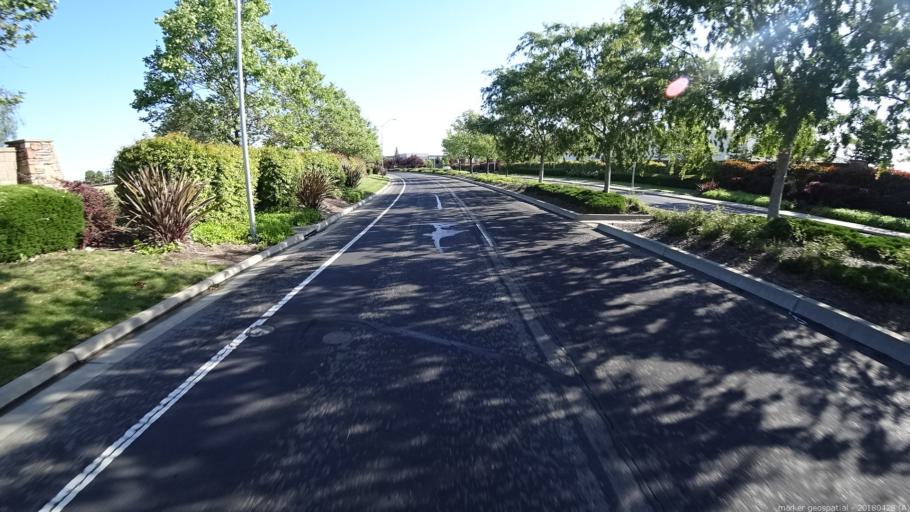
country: US
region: California
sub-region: Yolo County
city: West Sacramento
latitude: 38.5469
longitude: -121.5672
